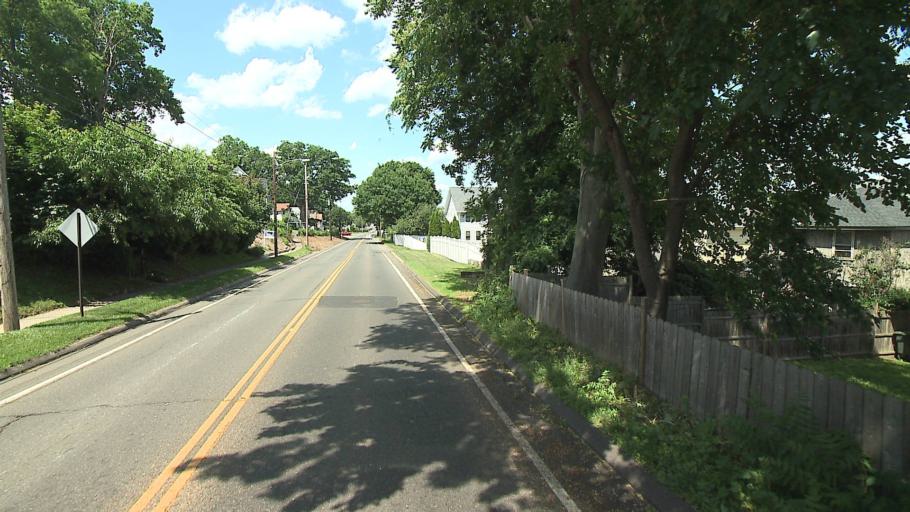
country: US
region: Connecticut
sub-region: New Haven County
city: Woodmont
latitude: 41.2184
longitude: -73.0067
